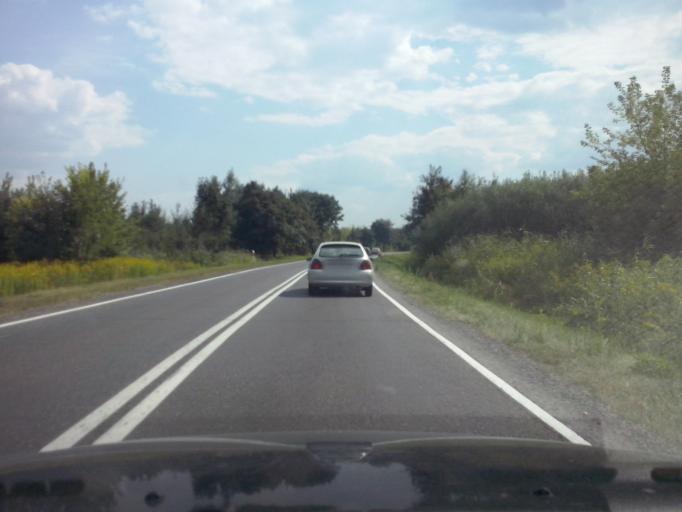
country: PL
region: Subcarpathian Voivodeship
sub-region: Powiat nizanski
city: Rudnik nad Sanem
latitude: 50.4662
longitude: 22.2424
